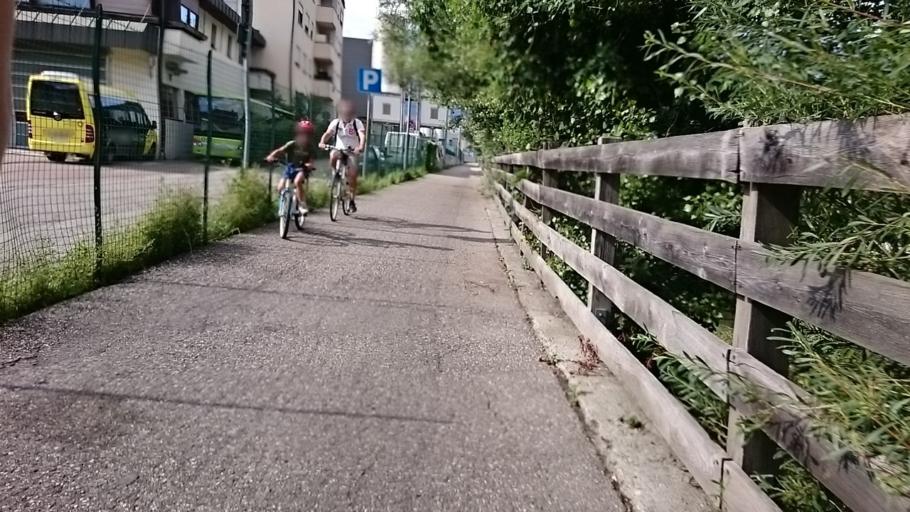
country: IT
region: Trentino-Alto Adige
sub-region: Bolzano
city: Leone-Santa Elisabetta
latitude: 46.7279
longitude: 11.6536
